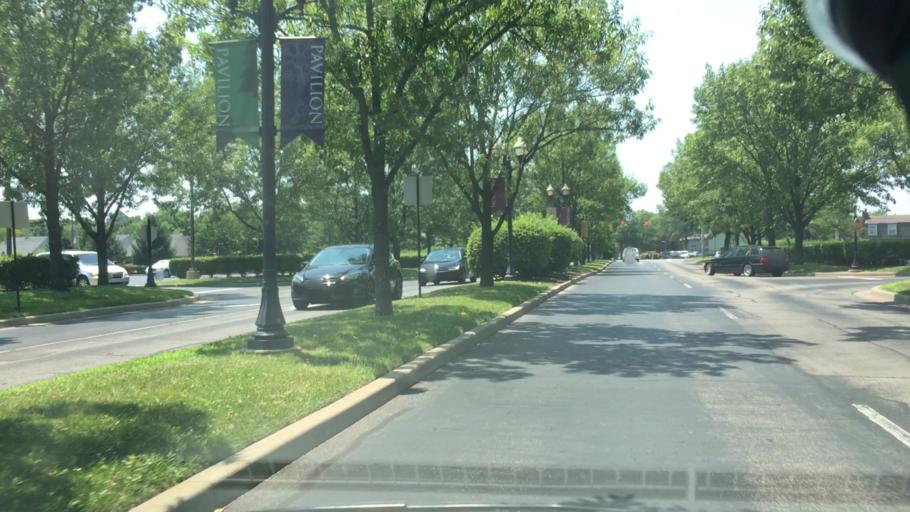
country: US
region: Indiana
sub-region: Vanderburgh County
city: Melody Hill
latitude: 37.9745
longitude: -87.4726
